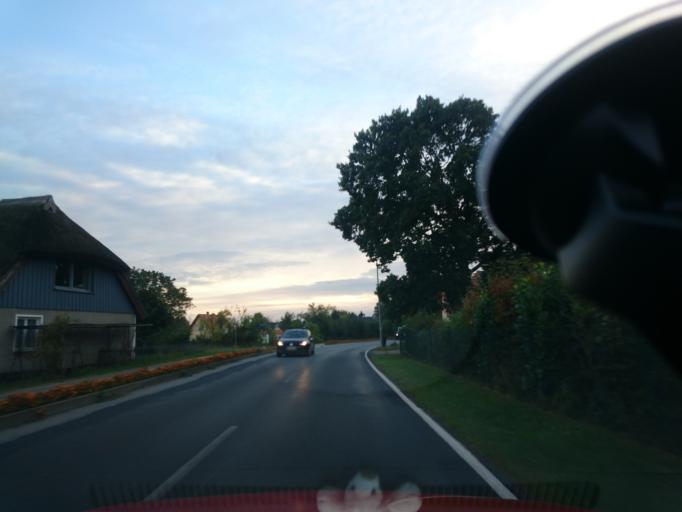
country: DE
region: Mecklenburg-Vorpommern
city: Born
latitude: 54.3636
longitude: 12.6068
